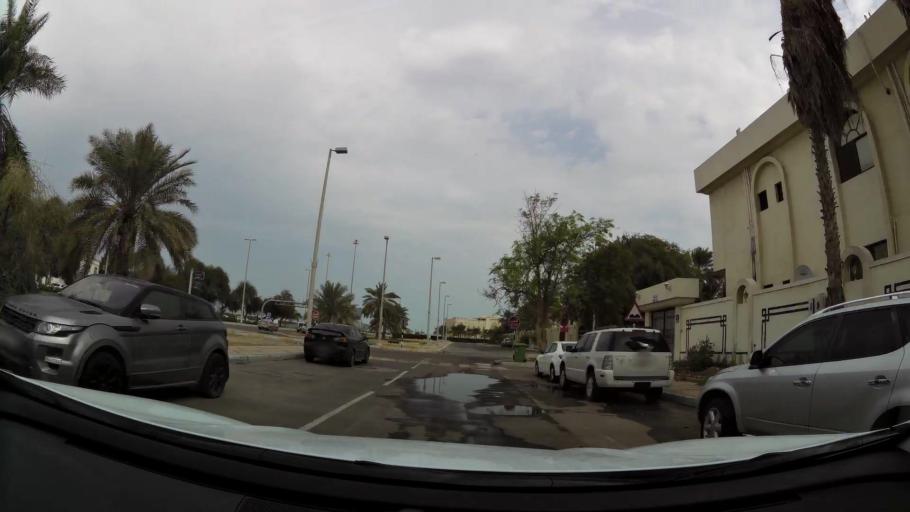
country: AE
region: Abu Dhabi
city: Abu Dhabi
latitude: 24.4431
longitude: 54.4319
